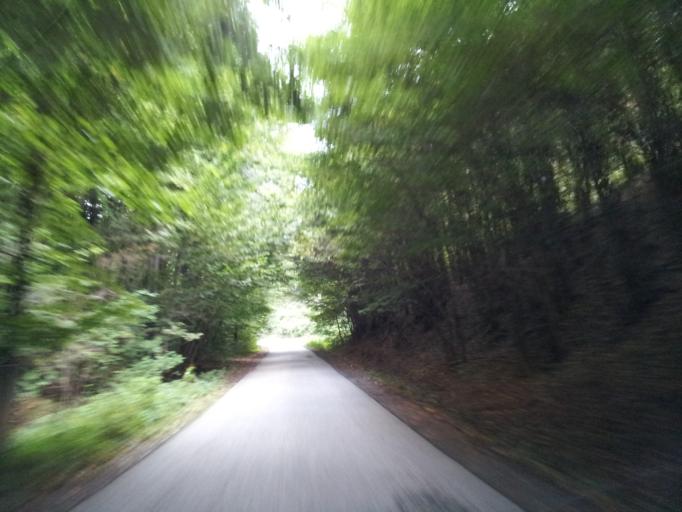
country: HU
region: Pest
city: Kismaros
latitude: 47.8865
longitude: 18.9593
